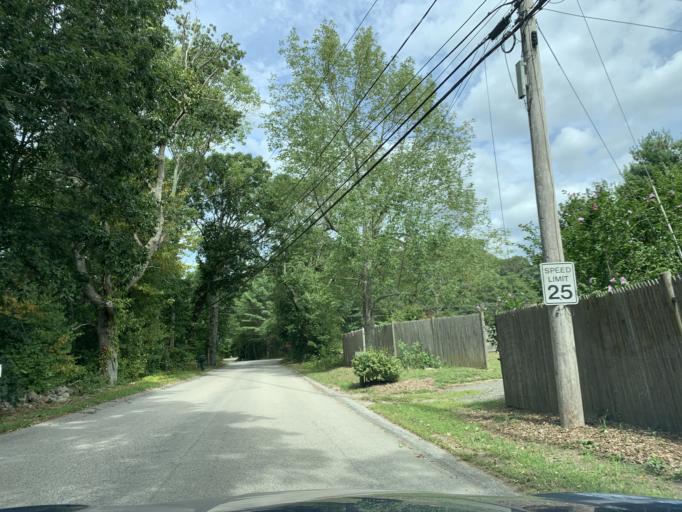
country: US
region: Rhode Island
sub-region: Washington County
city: Exeter
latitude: 41.5390
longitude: -71.6158
